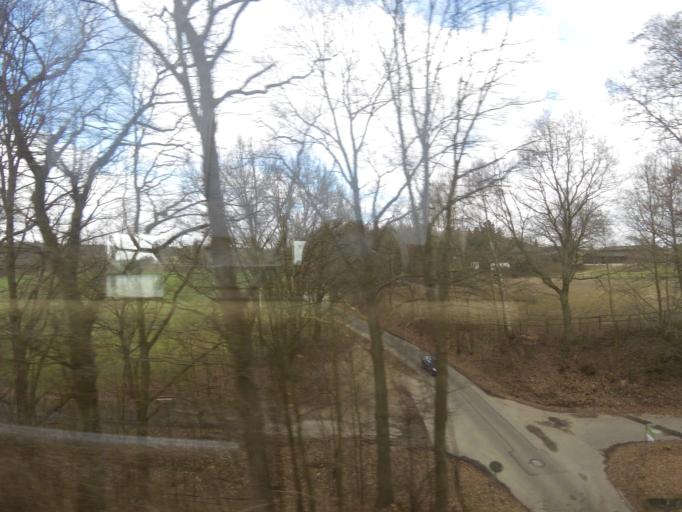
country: DE
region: Lower Saxony
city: Seevetal
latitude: 53.3975
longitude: 9.9686
